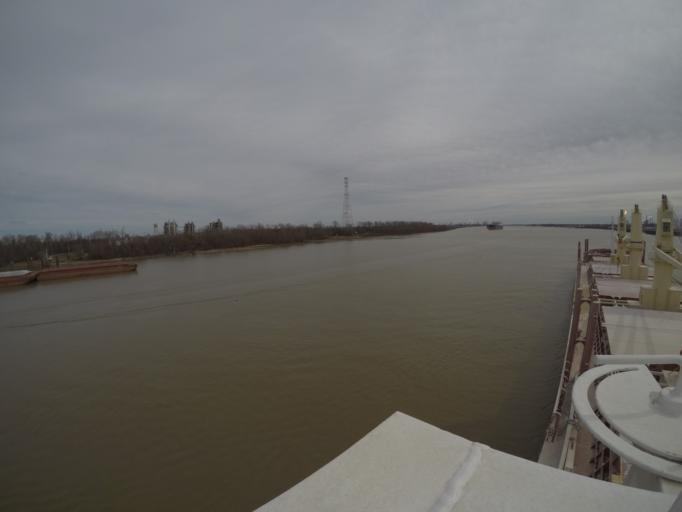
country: US
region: Louisiana
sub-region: Saint Charles Parish
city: Montz
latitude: 29.9991
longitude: -90.4669
